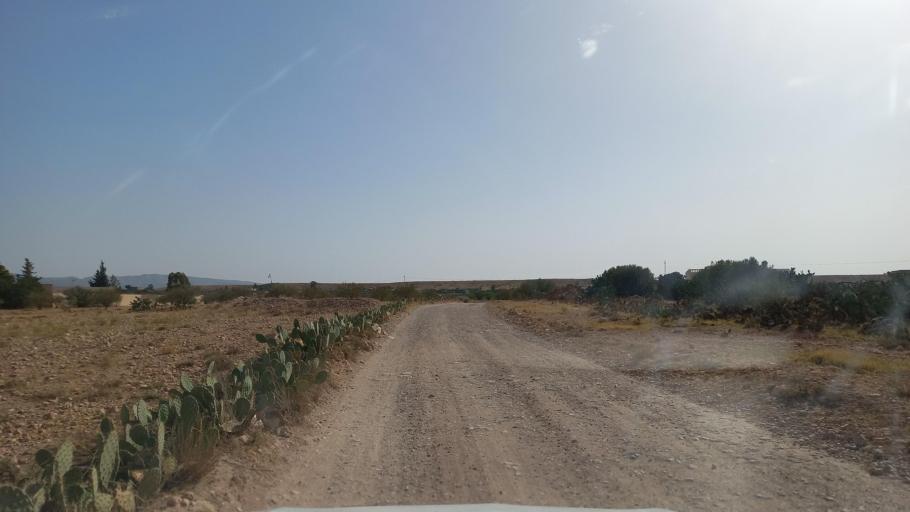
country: TN
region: Al Qasrayn
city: Kasserine
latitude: 35.2674
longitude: 8.9344
